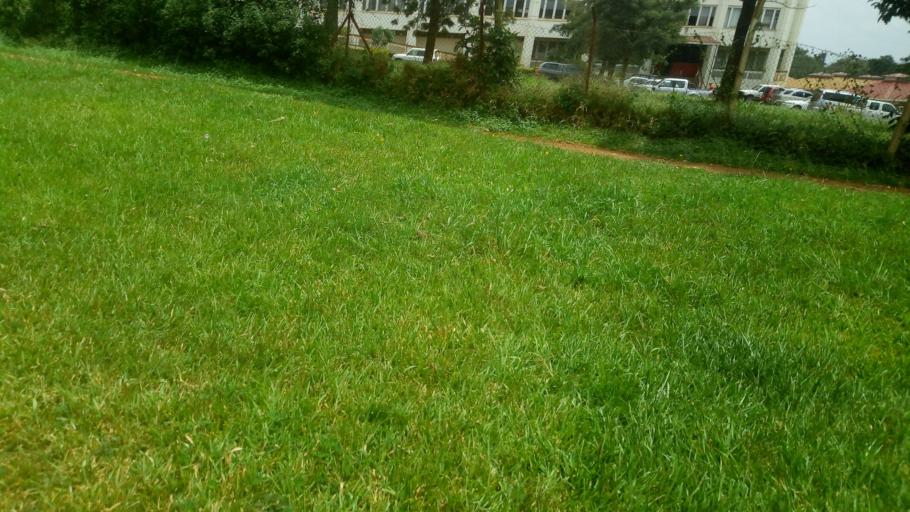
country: UG
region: Central Region
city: Kampala Central Division
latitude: 0.3393
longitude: 32.5684
